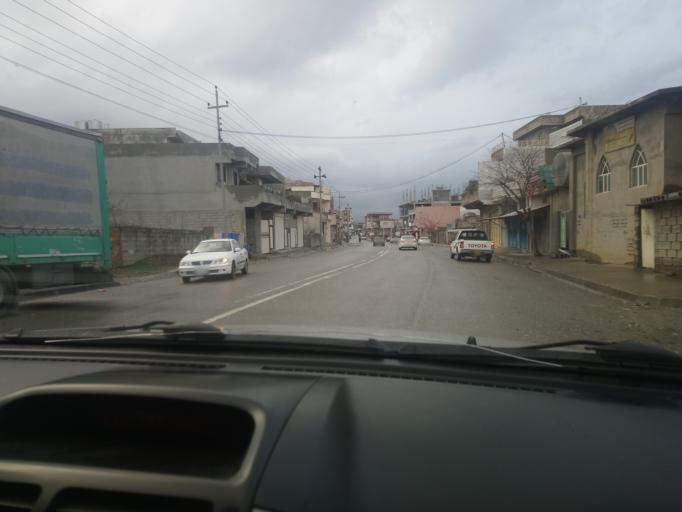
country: IQ
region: As Sulaymaniyah
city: Qeladize
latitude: 36.1842
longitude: 45.1306
